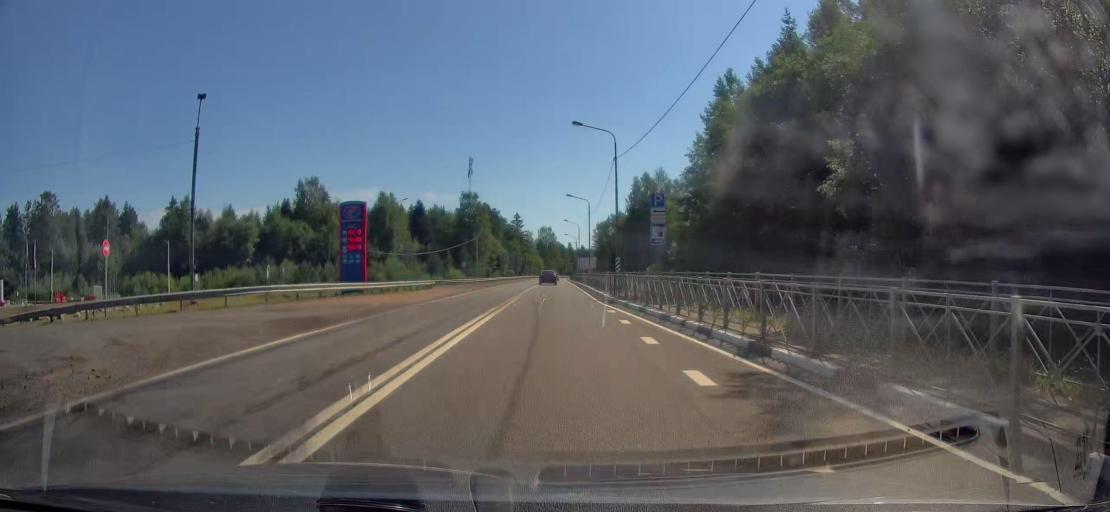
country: RU
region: Leningrad
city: Yefimovskiy
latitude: 59.3467
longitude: 34.8625
